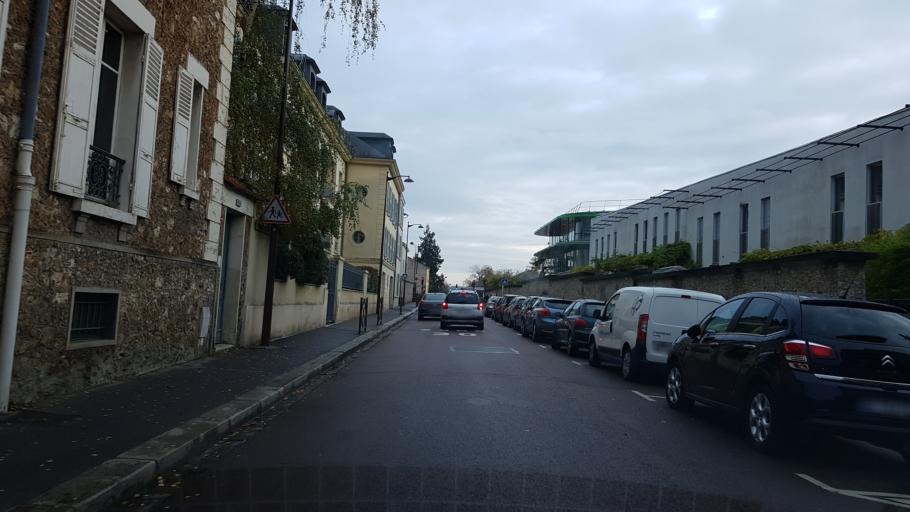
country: FR
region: Ile-de-France
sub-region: Departement des Yvelines
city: Versailles
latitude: 48.8036
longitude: 2.1446
